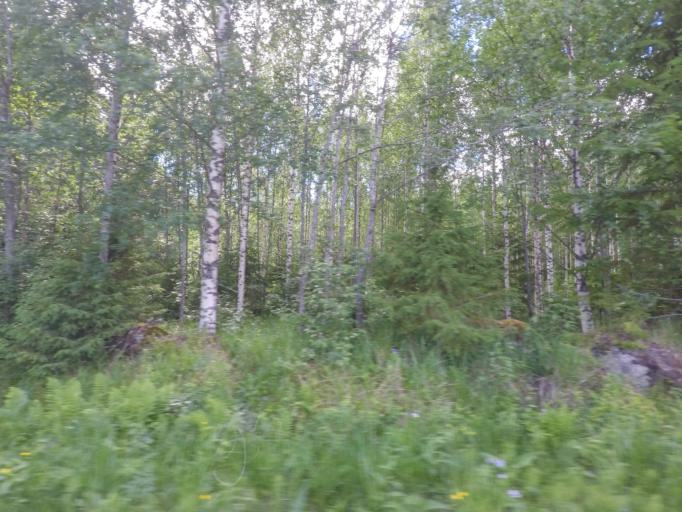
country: FI
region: Central Finland
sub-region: Jyvaeskylae
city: Hankasalmi
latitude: 62.4144
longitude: 26.6425
